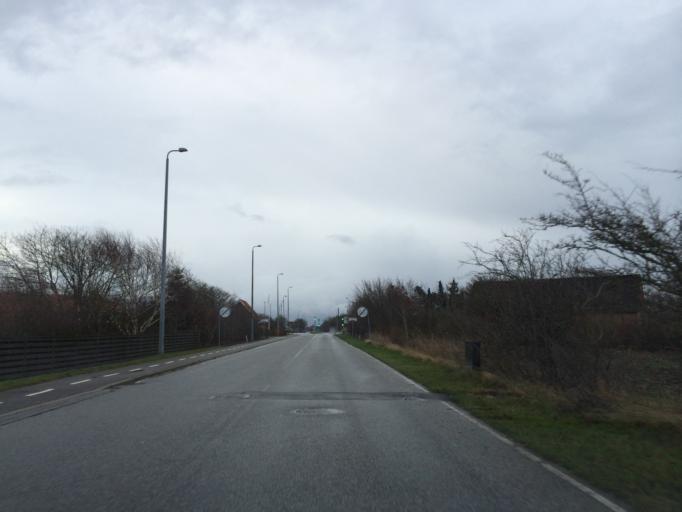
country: DK
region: Central Jutland
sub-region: Ringkobing-Skjern Kommune
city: Skjern
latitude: 55.9568
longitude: 8.4836
